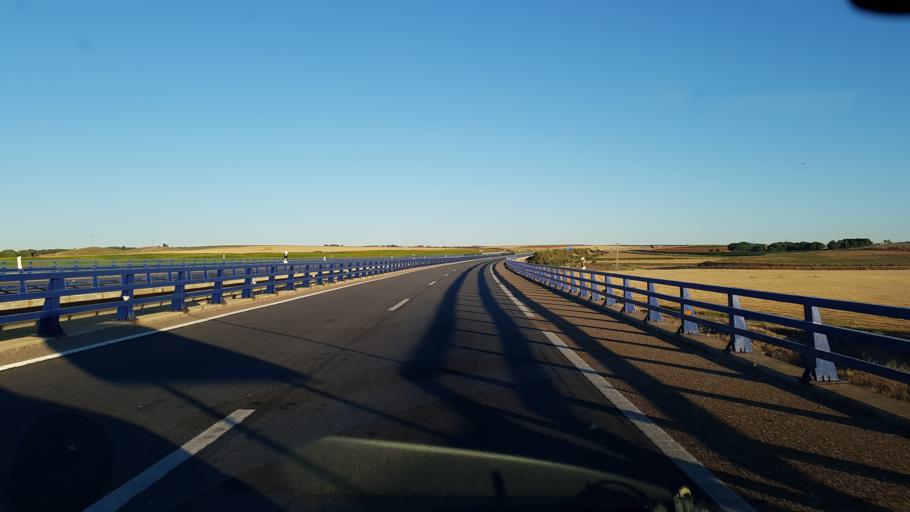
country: ES
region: Castille and Leon
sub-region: Provincia de Zamora
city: Morales de Toro
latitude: 41.5273
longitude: -5.2696
